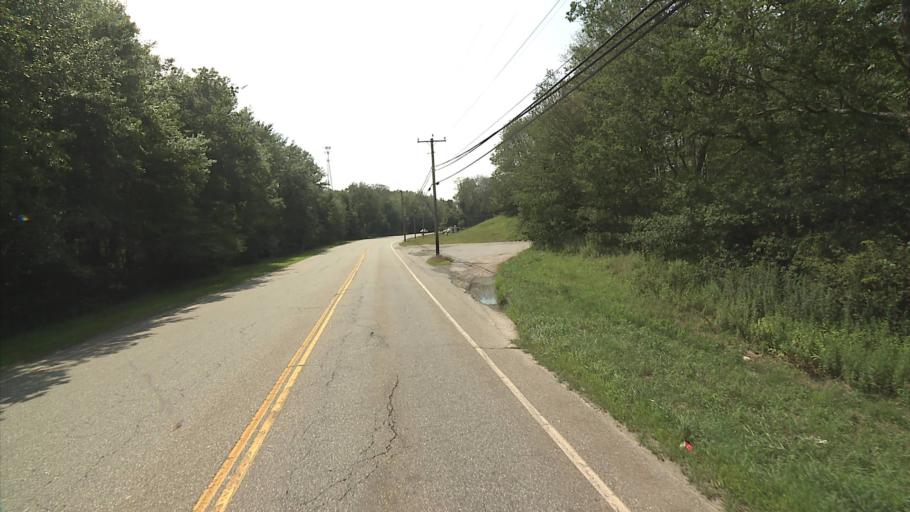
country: US
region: Connecticut
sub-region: New London County
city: Montville Center
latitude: 41.4714
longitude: -72.2708
